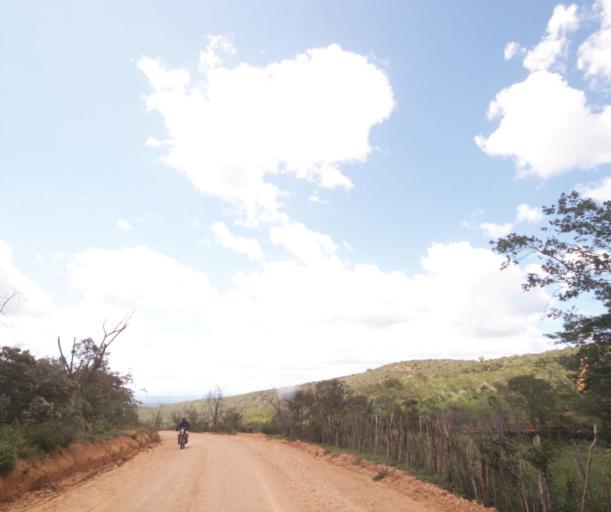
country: BR
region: Bahia
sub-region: Pocoes
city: Pocoes
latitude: -14.2972
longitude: -40.6702
